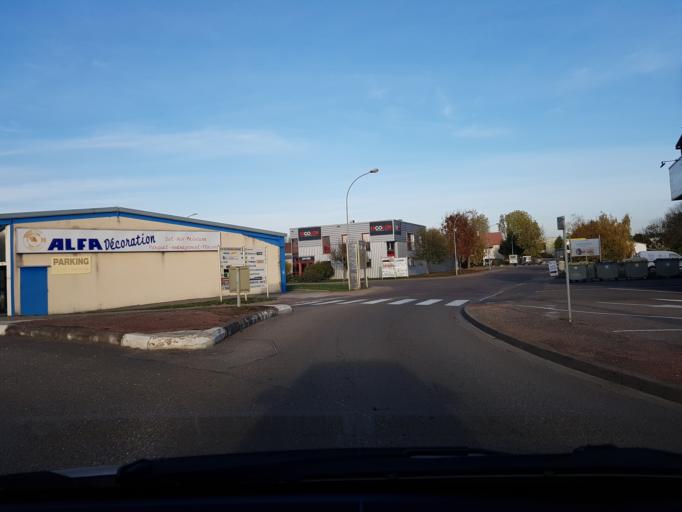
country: FR
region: Bourgogne
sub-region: Departement de la Cote-d'Or
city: Ahuy
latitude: 47.3556
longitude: 5.0349
